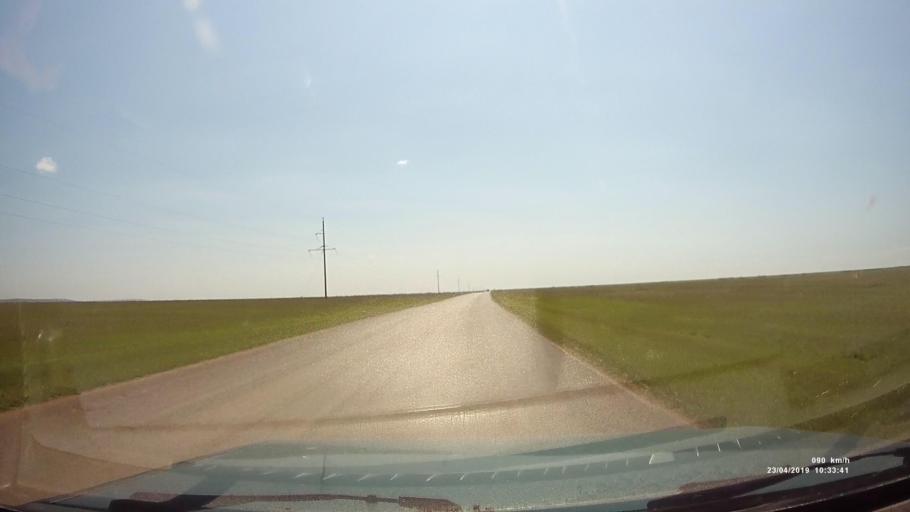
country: RU
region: Kalmykiya
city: Yashalta
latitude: 46.5714
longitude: 42.6003
